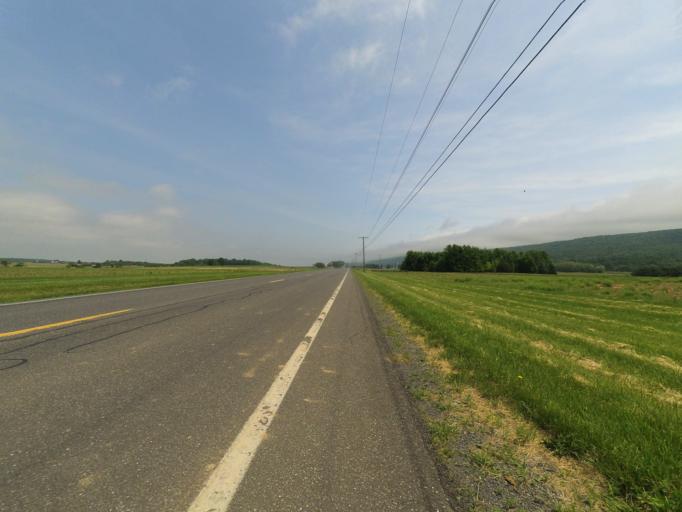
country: US
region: Pennsylvania
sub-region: Centre County
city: Pine Grove Mills
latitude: 40.7137
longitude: -77.9500
